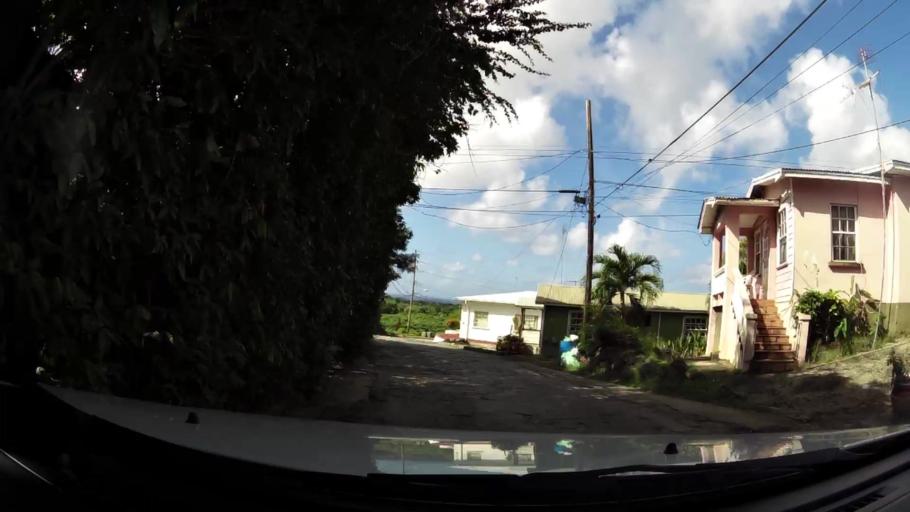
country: BB
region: Saint Lucy
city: Checker Hall
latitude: 13.2638
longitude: -59.6212
